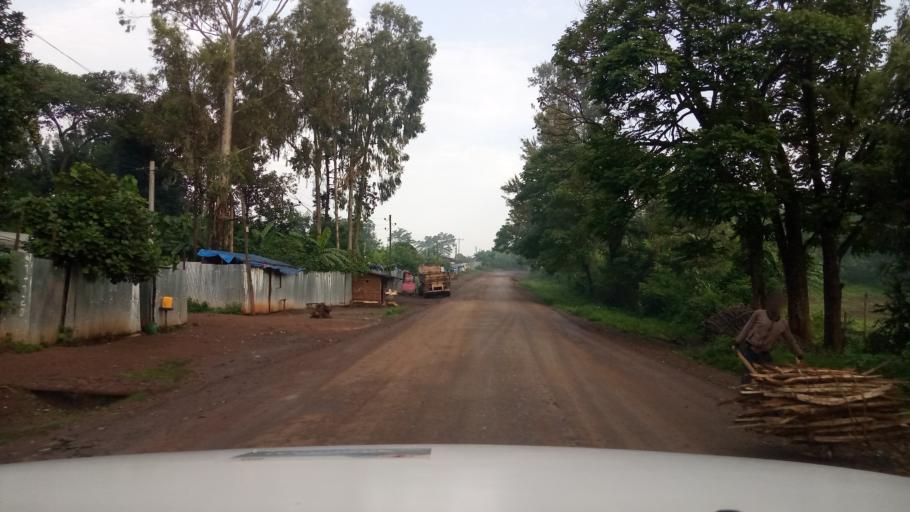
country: ET
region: Oromiya
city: Jima
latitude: 7.7015
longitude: 36.8091
